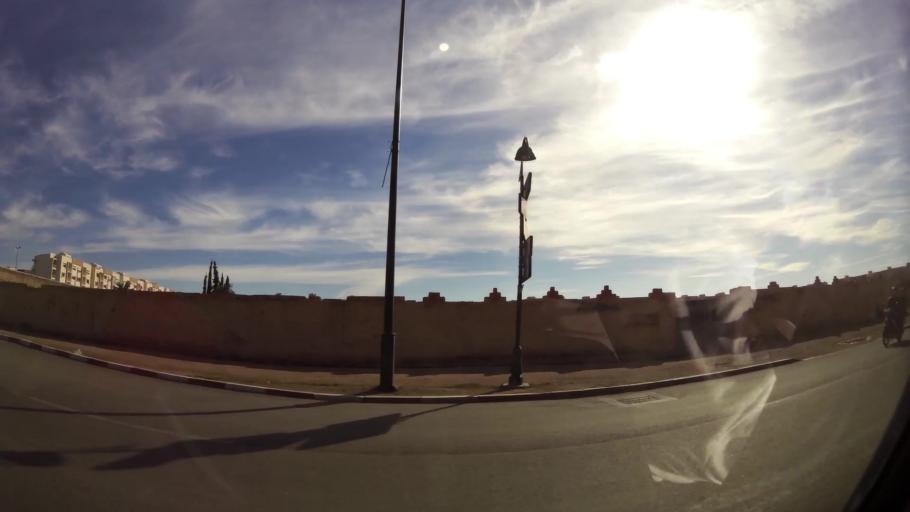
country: MA
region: Marrakech-Tensift-Al Haouz
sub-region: Marrakech
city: Marrakesh
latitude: 31.6628
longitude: -8.0304
